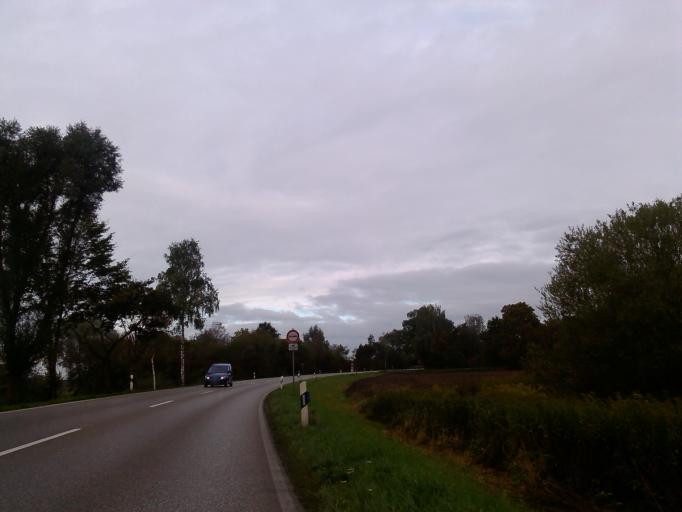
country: DE
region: Bavaria
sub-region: Upper Bavaria
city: Olching
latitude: 48.1975
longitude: 11.3496
